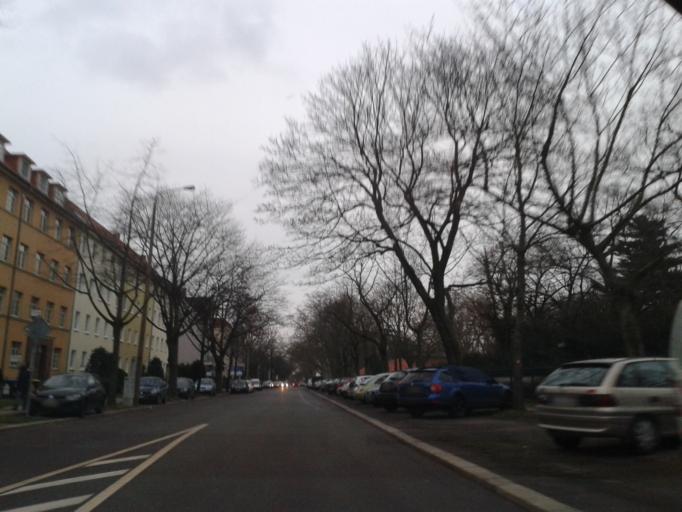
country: DE
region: Saxony-Anhalt
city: Halle (Saale)
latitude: 51.4628
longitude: 11.9741
